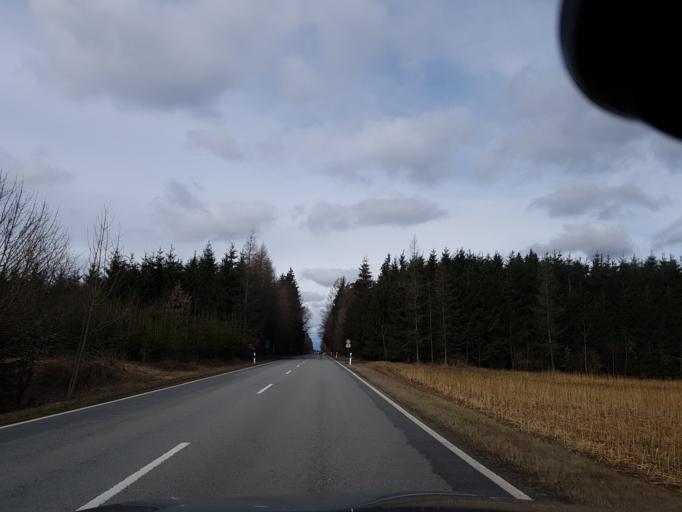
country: DE
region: Bavaria
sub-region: Upper Bavaria
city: Aying
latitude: 47.9806
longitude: 11.7523
